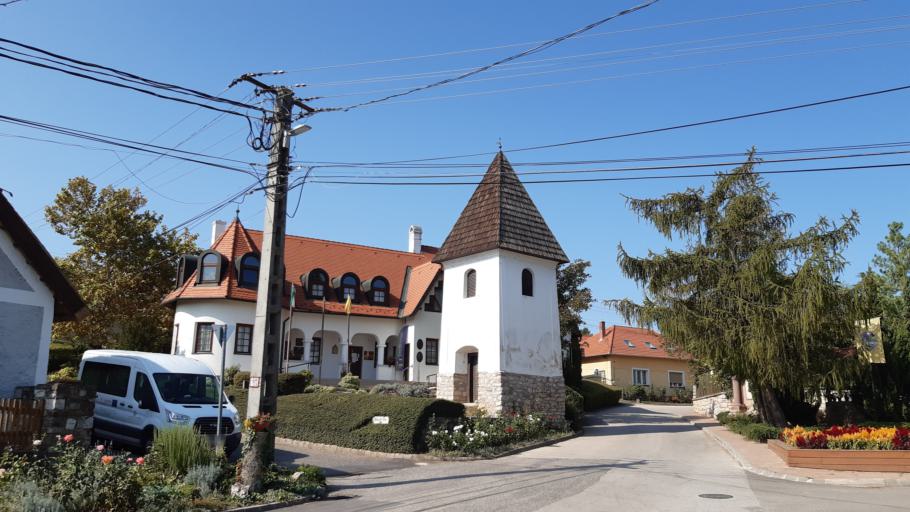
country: HU
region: Veszprem
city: Csopak
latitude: 46.9842
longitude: 17.9400
